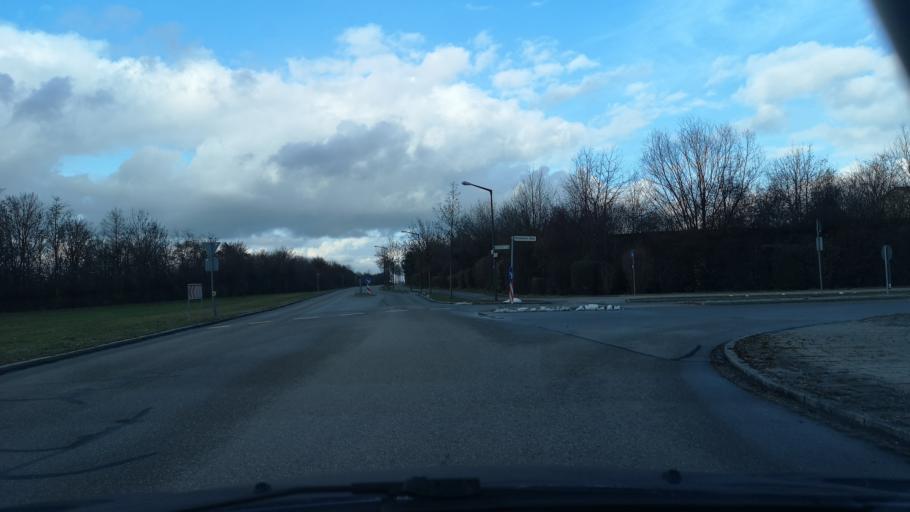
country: DE
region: Bavaria
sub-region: Upper Bavaria
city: Pliening
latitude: 48.1732
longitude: 11.7910
